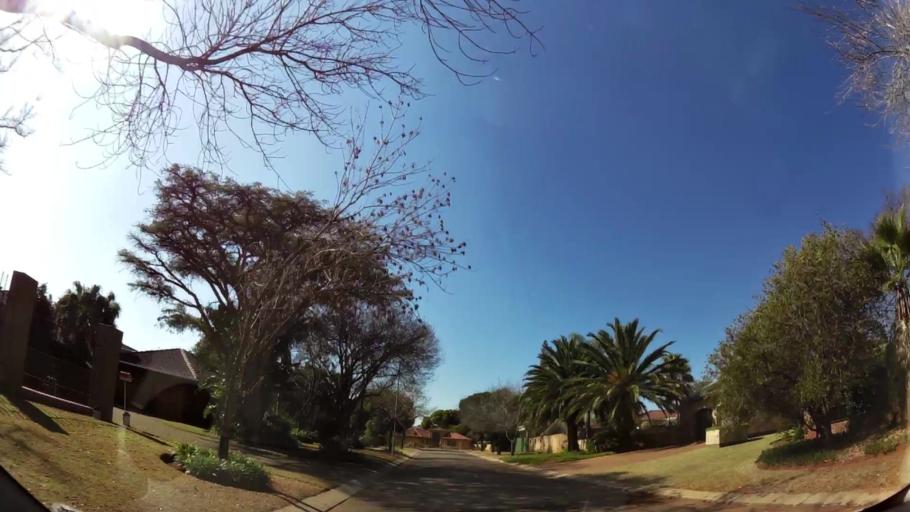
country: ZA
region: Gauteng
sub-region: City of Tshwane Metropolitan Municipality
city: Centurion
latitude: -25.8250
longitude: 28.2392
